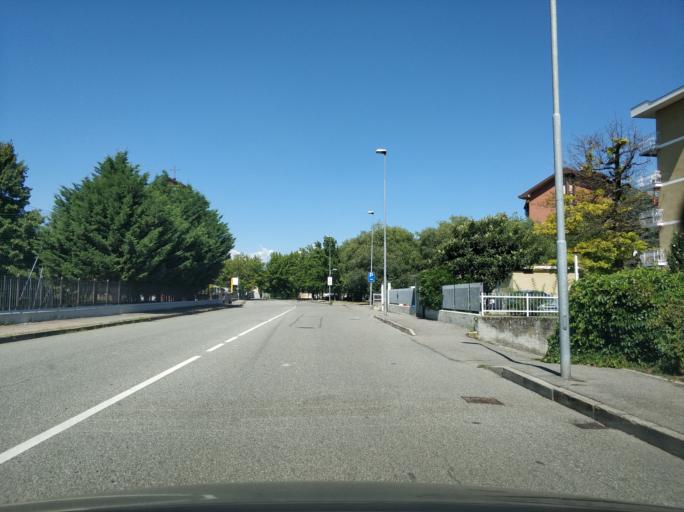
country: IT
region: Piedmont
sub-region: Provincia di Torino
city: Settimo Torinese
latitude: 45.1413
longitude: 7.7618
